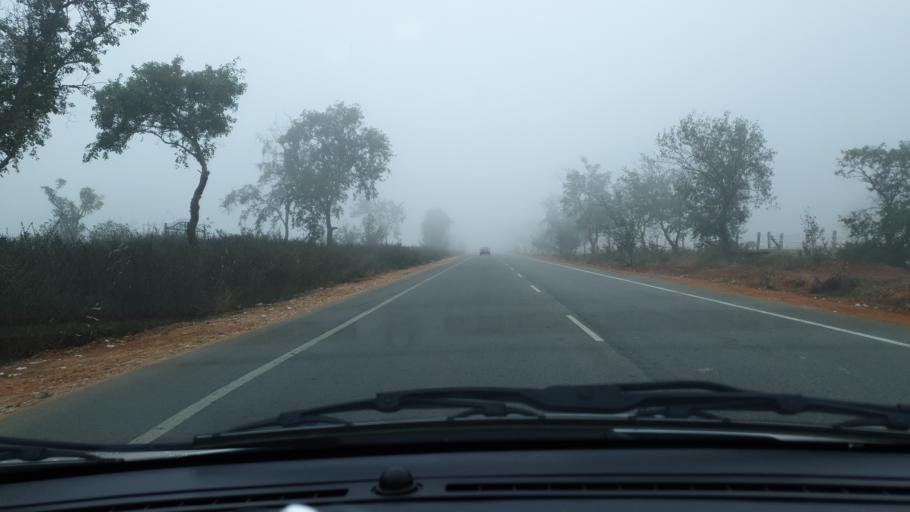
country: IN
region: Telangana
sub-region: Mahbubnagar
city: Nagar Karnul
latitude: 16.6565
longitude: 78.5762
